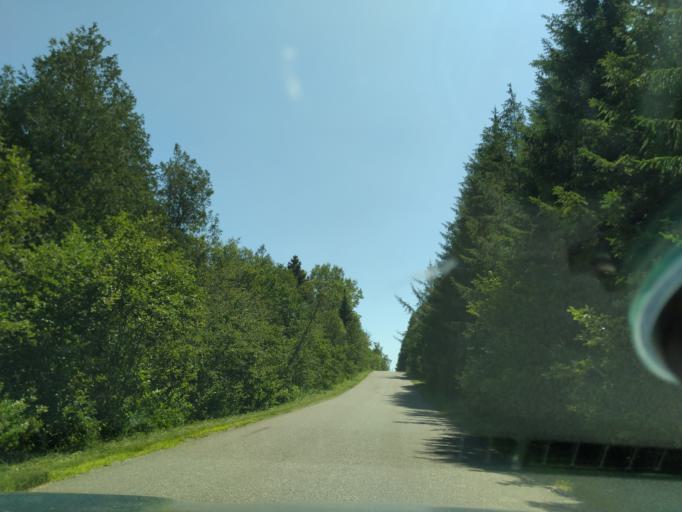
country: US
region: Maine
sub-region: Washington County
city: Eastport
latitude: 44.8346
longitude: -67.0094
